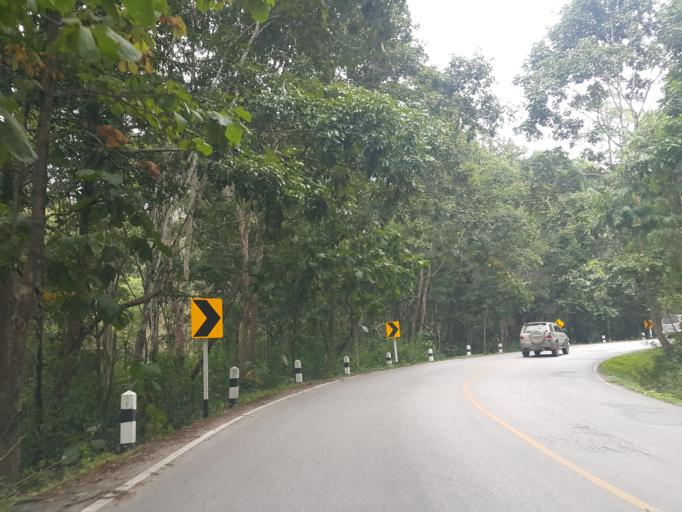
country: TH
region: Mae Hong Son
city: Mae Hi
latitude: 19.2663
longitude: 98.5168
